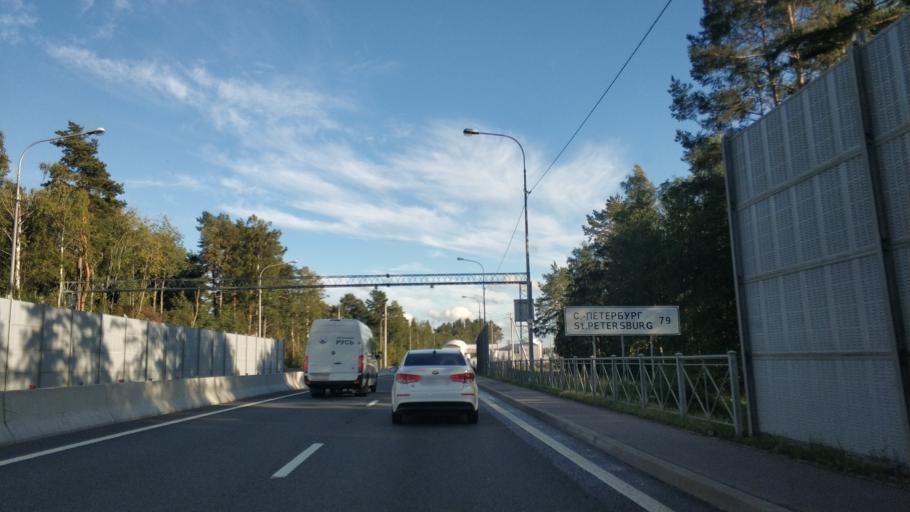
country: RU
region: Leningrad
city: Sapernoye
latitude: 60.6780
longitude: 30.0086
